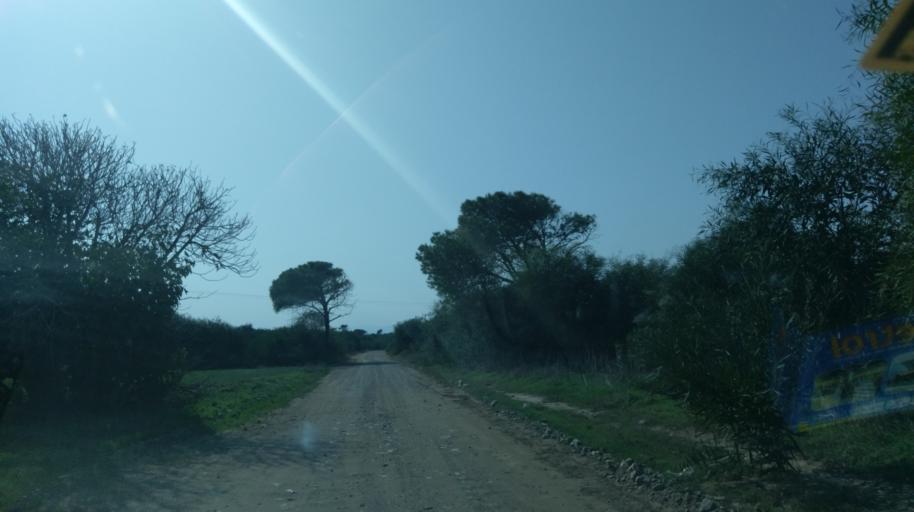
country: CY
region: Lefkosia
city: Morfou
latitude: 35.2905
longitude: 32.9499
